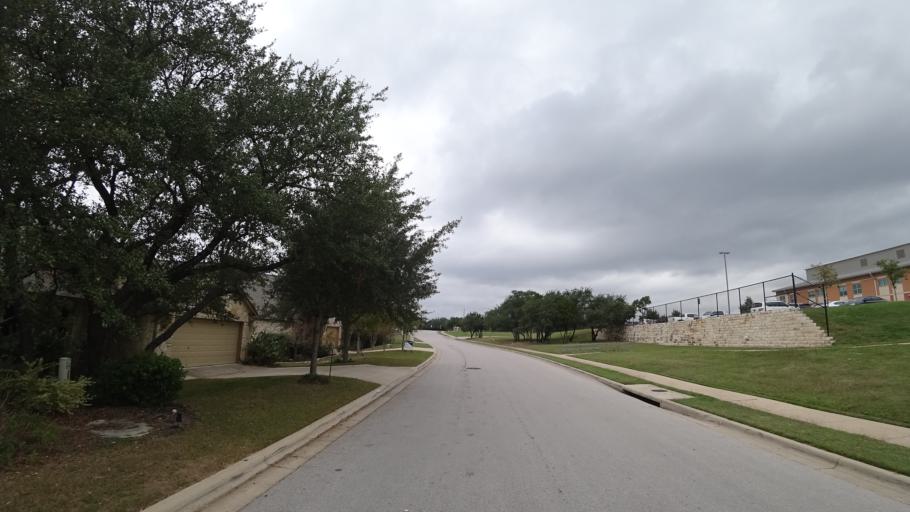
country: US
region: Texas
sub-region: Travis County
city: Bee Cave
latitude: 30.3450
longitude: -97.9164
